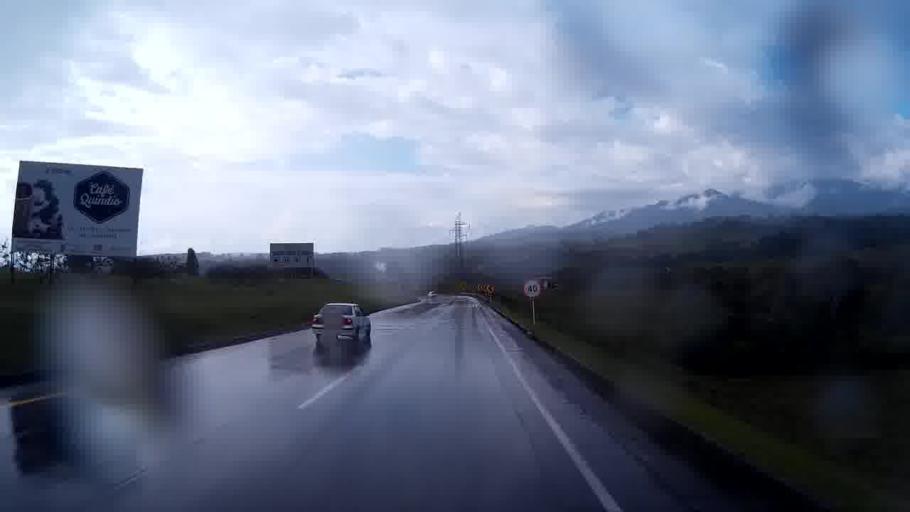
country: CO
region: Quindio
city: Filandia
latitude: 4.6864
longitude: -75.6065
